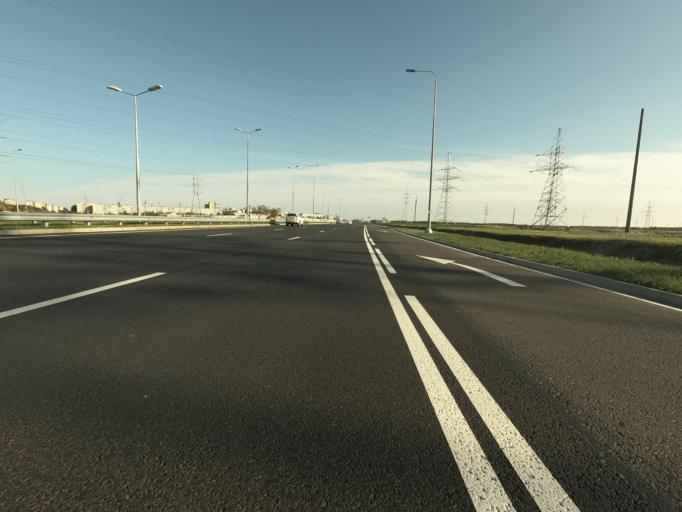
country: RU
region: St.-Petersburg
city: Kolpino
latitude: 59.7418
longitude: 30.5446
